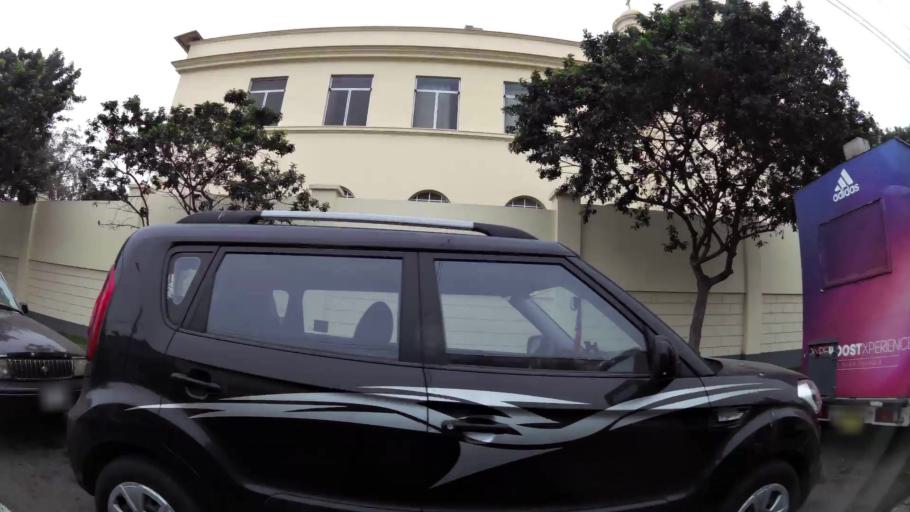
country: PE
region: Lima
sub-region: Lima
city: San Isidro
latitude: -12.0943
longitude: -77.0295
